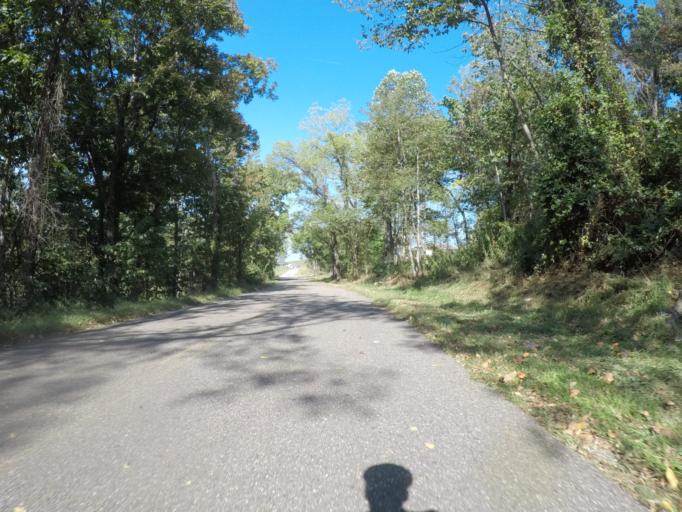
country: US
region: West Virginia
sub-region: Cabell County
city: Lesage
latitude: 38.6441
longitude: -82.4130
